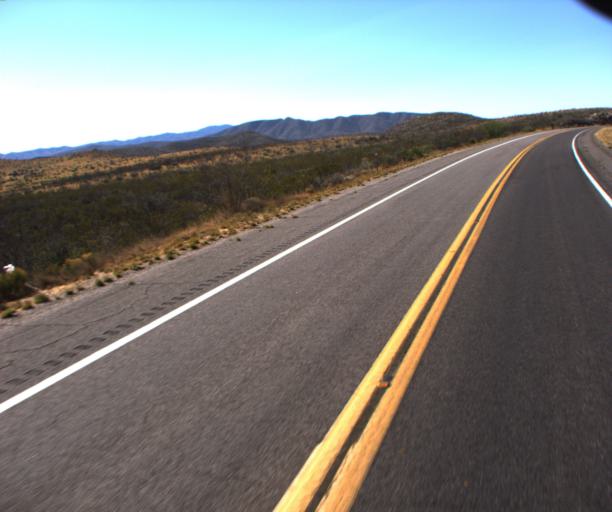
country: US
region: Arizona
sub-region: Cochise County
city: Tombstone
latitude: 31.6603
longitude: -110.0311
